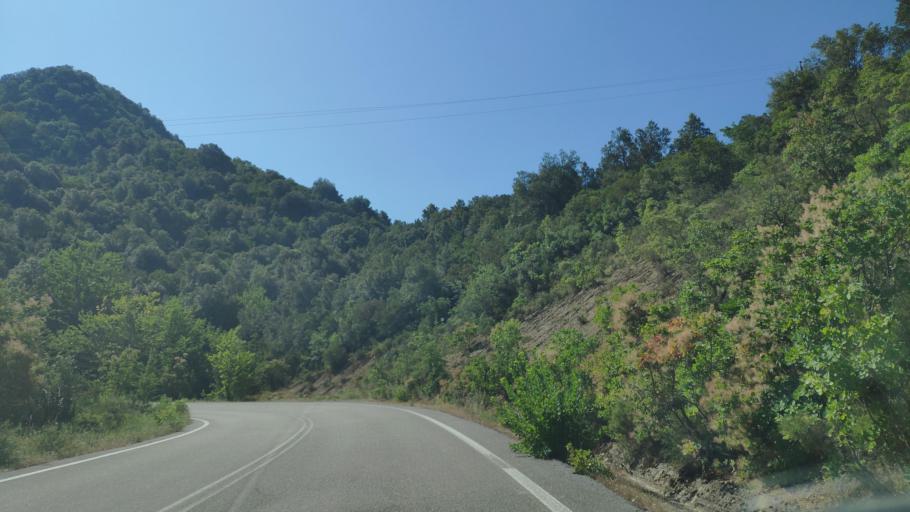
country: GR
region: West Greece
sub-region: Nomos Aitolias kai Akarnanias
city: Sardinia
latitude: 38.9209
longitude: 21.3922
